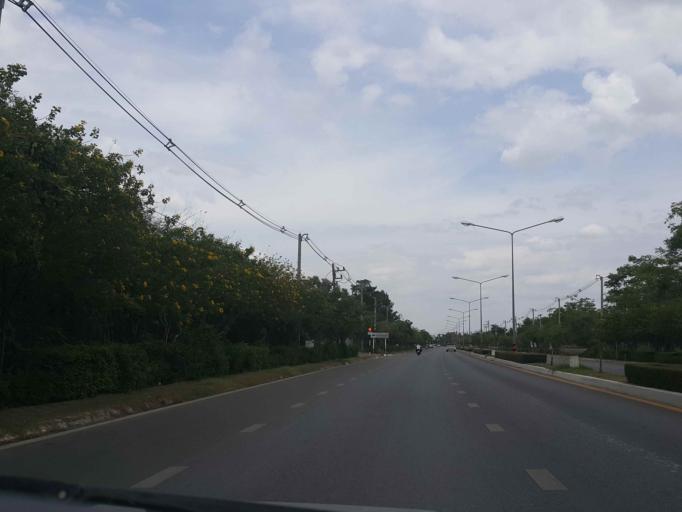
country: TH
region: Chiang Mai
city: Hang Dong
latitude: 18.7334
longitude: 98.9389
